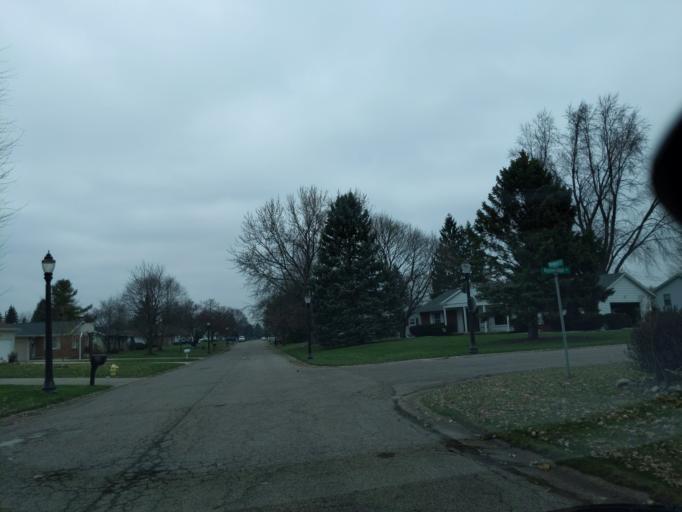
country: US
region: Michigan
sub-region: Eaton County
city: Waverly
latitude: 42.7274
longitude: -84.6318
